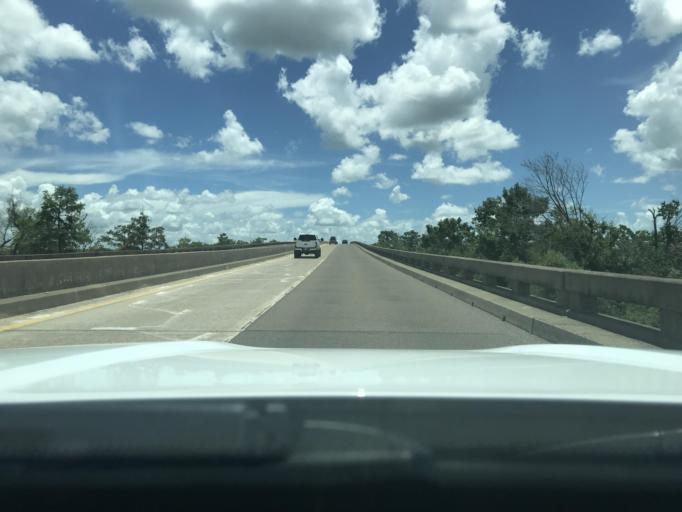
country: US
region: Louisiana
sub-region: Calcasieu Parish
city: Moss Bluff
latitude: 30.2893
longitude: -93.1908
